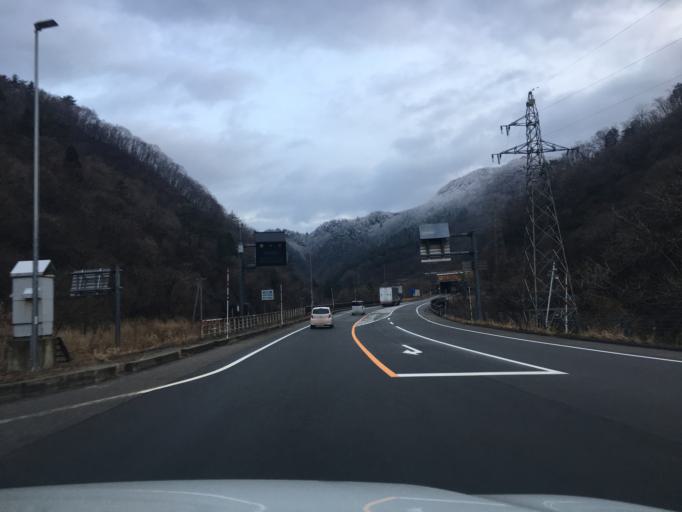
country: JP
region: Niigata
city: Murakami
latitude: 38.4000
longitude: 139.5565
